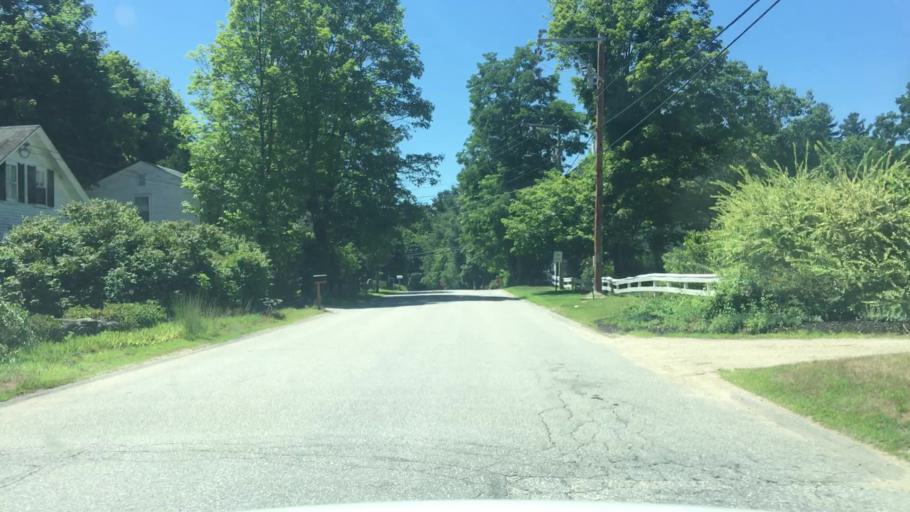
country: US
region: New Hampshire
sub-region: Merrimack County
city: Hopkinton
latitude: 43.1929
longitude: -71.6744
